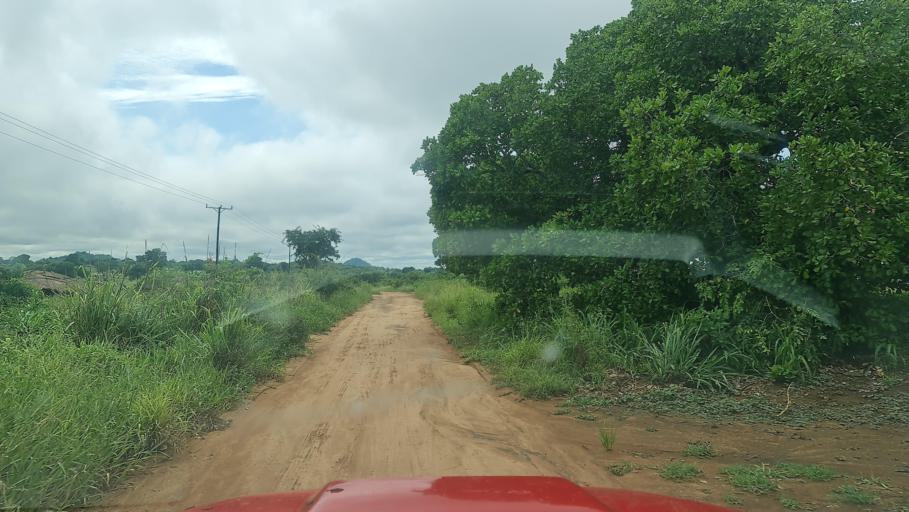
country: MW
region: Southern Region
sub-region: Nsanje District
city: Nsanje
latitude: -17.1842
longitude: 35.9152
